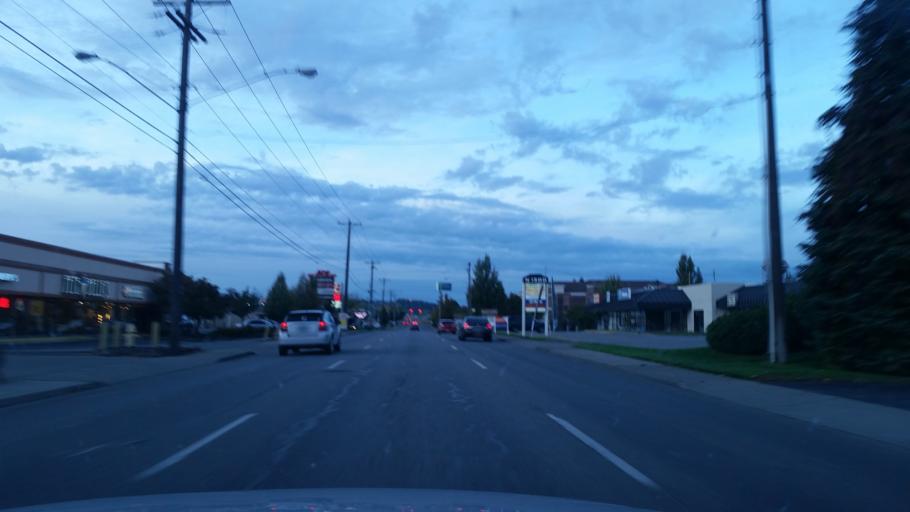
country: US
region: Washington
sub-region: Spokane County
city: Dishman
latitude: 47.6685
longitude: -117.2816
